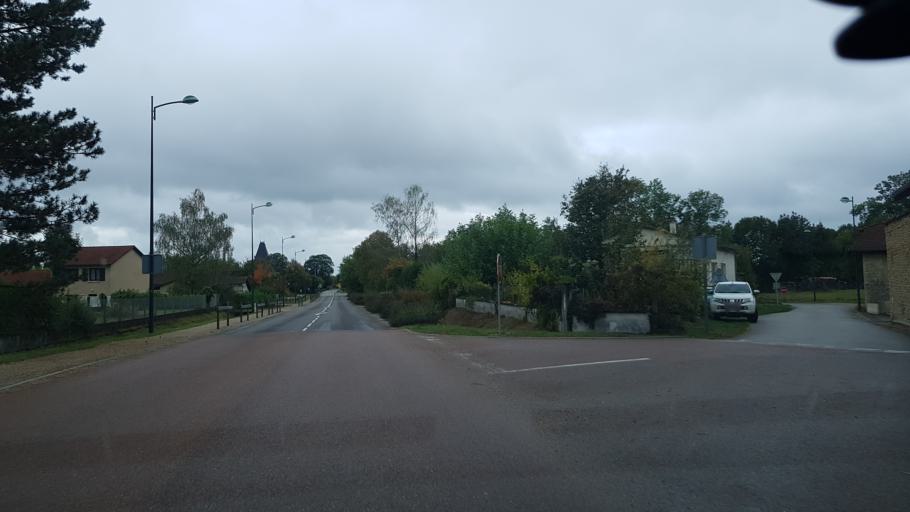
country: FR
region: Rhone-Alpes
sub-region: Departement de l'Ain
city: Tossiat
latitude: 46.1427
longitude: 5.3219
